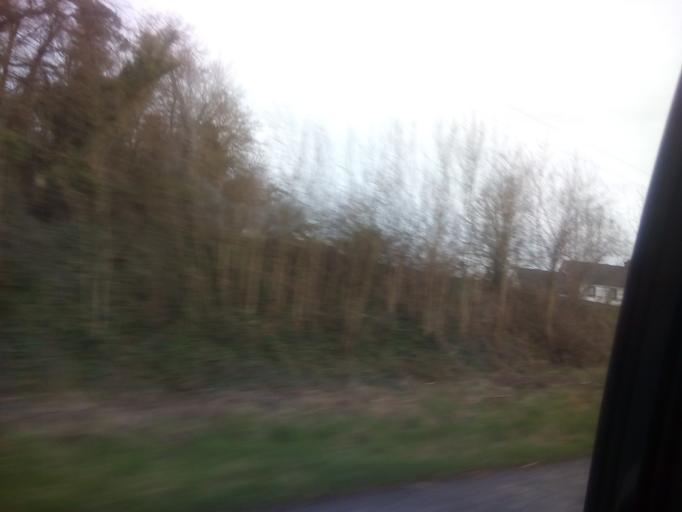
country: IE
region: Leinster
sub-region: Laois
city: Abbeyleix
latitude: 52.8563
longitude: -7.3853
